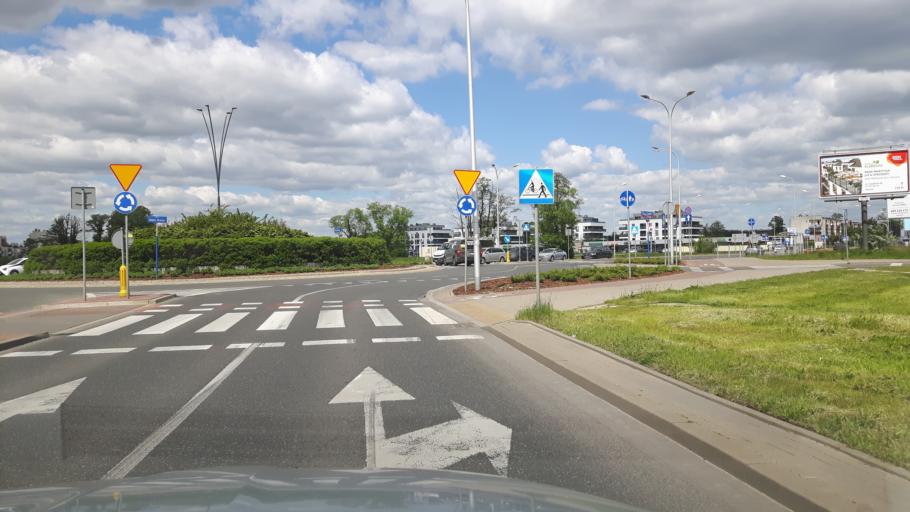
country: PL
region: Masovian Voivodeship
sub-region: Warszawa
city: Targowek
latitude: 52.3097
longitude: 21.0621
